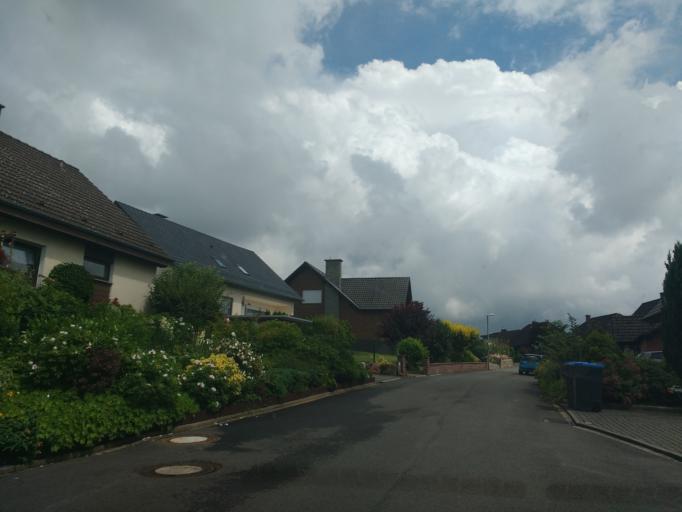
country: DE
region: North Rhine-Westphalia
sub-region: Regierungsbezirk Detmold
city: Blomberg
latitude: 51.9402
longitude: 9.1009
